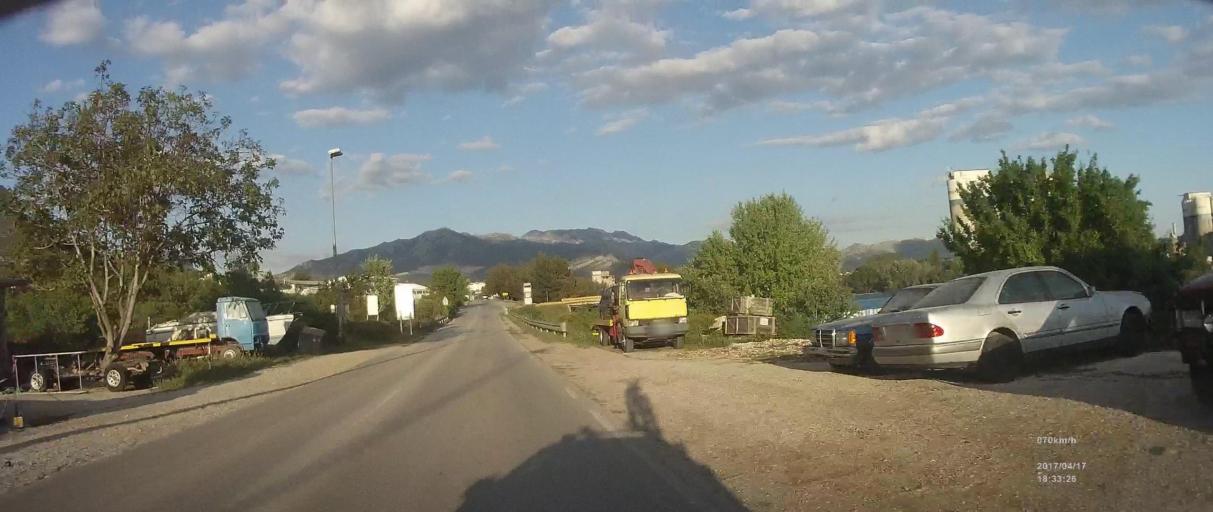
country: HR
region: Splitsko-Dalmatinska
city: Vranjic
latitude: 43.5413
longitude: 16.4595
